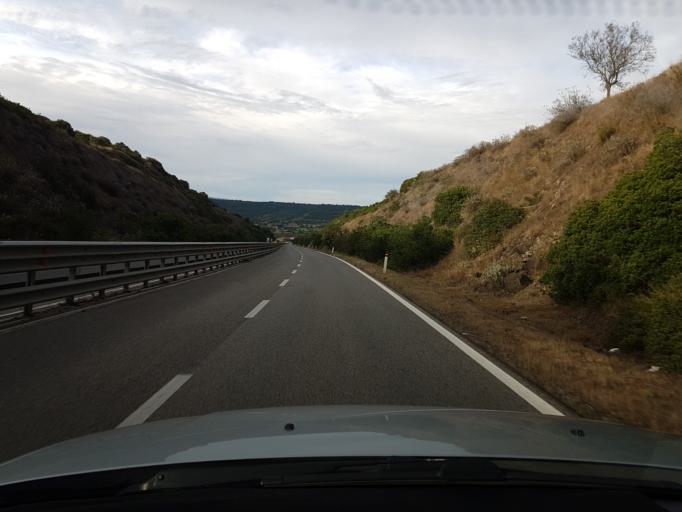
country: IT
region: Sardinia
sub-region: Provincia di Oristano
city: Soddi
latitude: 40.1348
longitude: 8.8677
